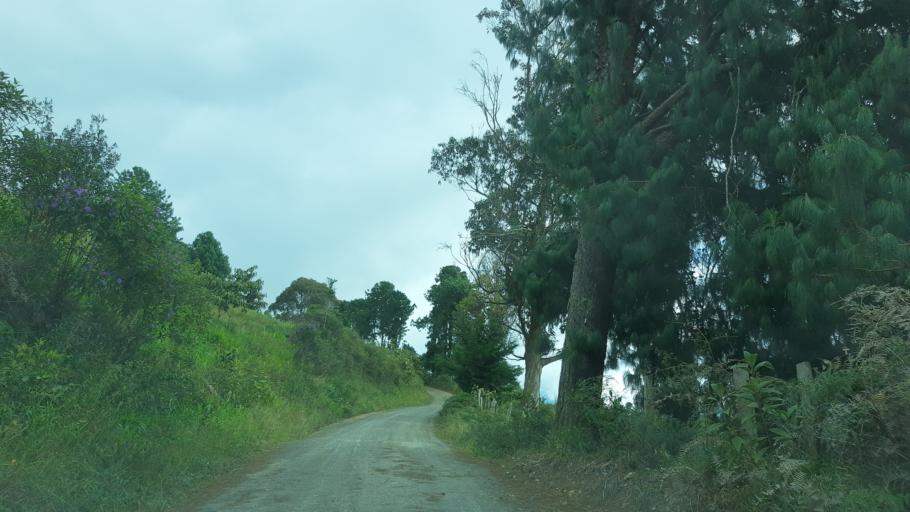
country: CO
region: Boyaca
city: Garagoa
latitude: 5.0016
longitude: -73.3376
